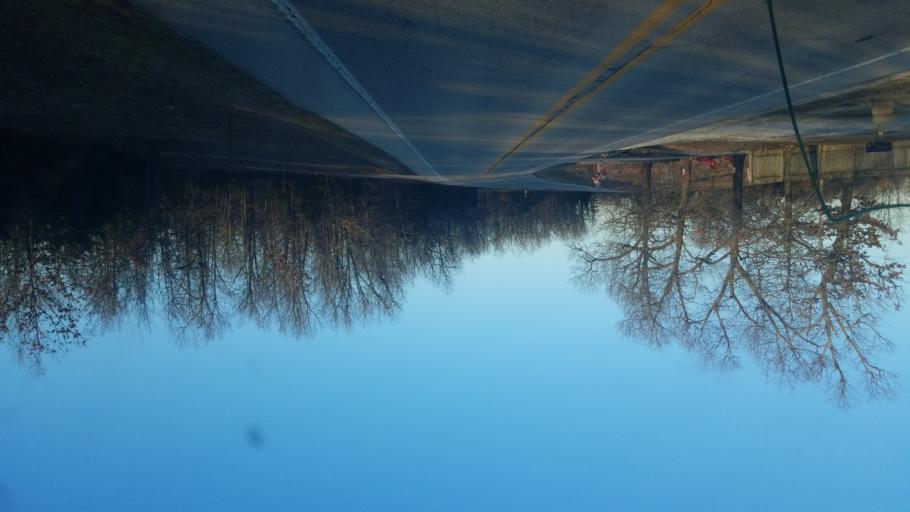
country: US
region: Arkansas
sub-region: Baxter County
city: Mountain Home
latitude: 36.3846
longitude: -92.1606
